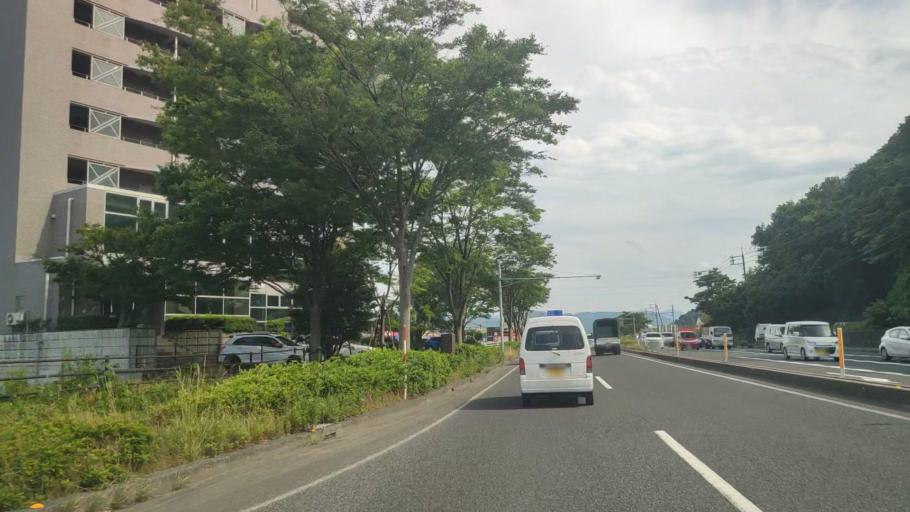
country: JP
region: Tottori
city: Tottori
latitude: 35.4983
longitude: 134.2022
